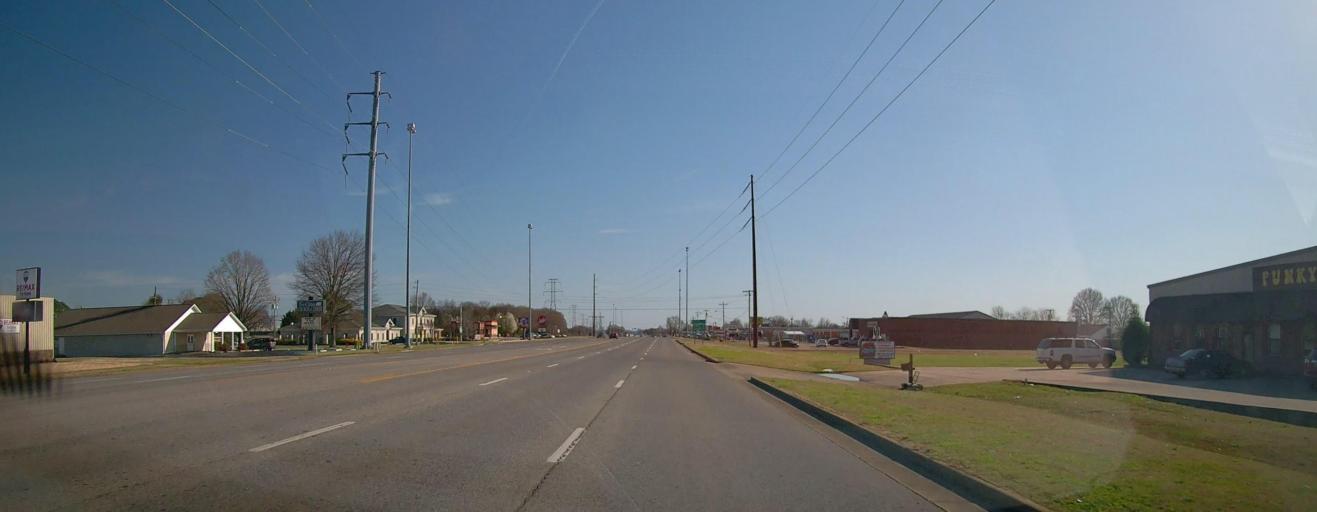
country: US
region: Alabama
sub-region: Colbert County
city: Muscle Shoals
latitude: 34.7492
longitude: -87.6353
